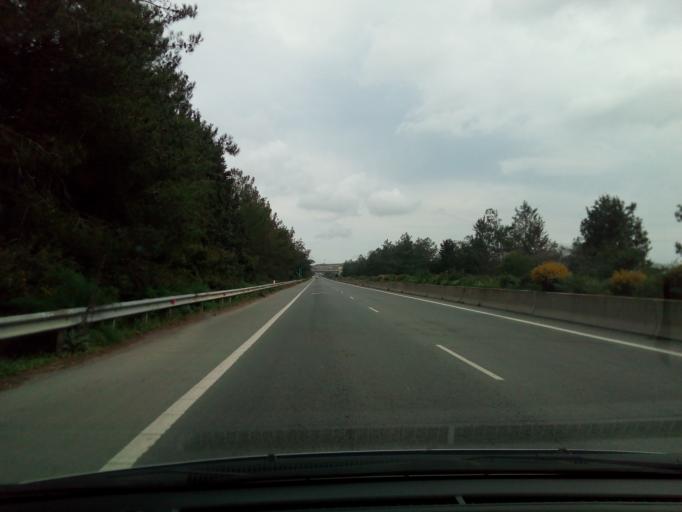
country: CY
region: Lefkosia
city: Lympia
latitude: 34.9960
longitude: 33.4414
